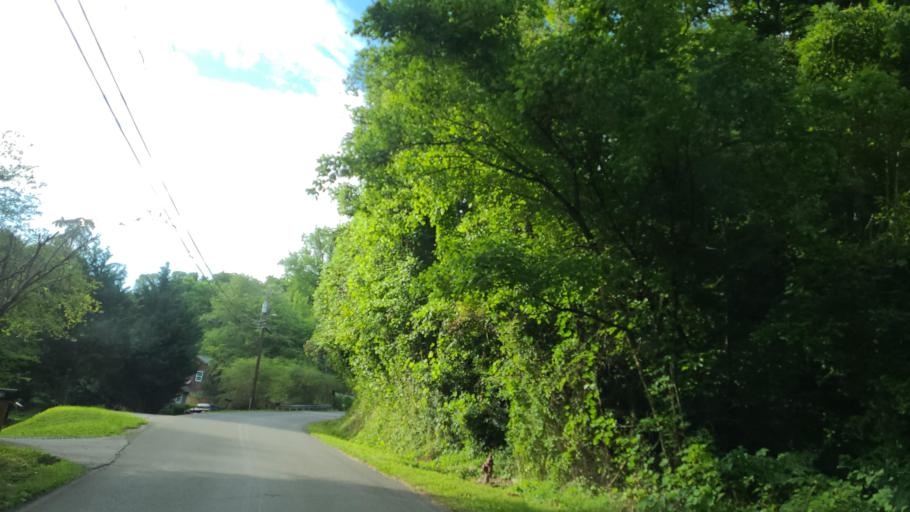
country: US
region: Georgia
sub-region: Gilmer County
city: Ellijay
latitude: 34.6982
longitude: -84.4872
